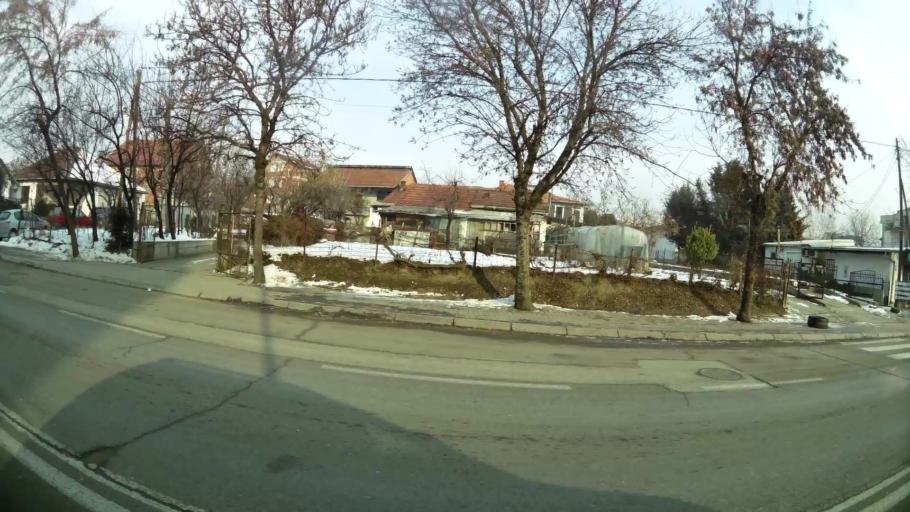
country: MK
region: Cair
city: Cair
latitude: 42.0135
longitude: 21.4400
